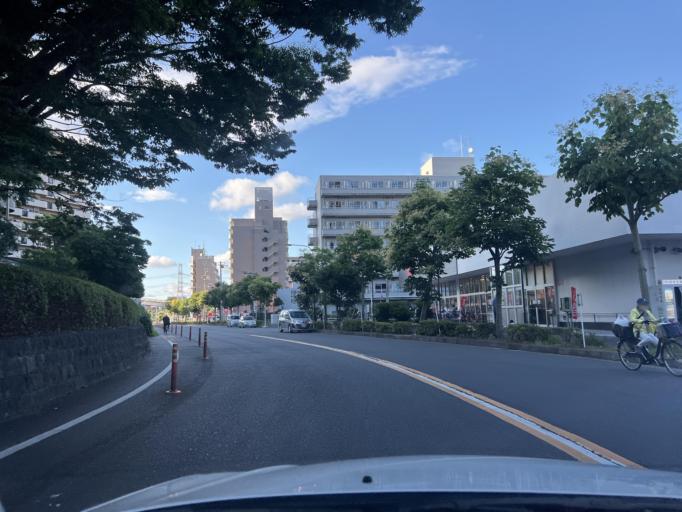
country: JP
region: Tokyo
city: Urayasu
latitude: 35.6457
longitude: 139.8719
